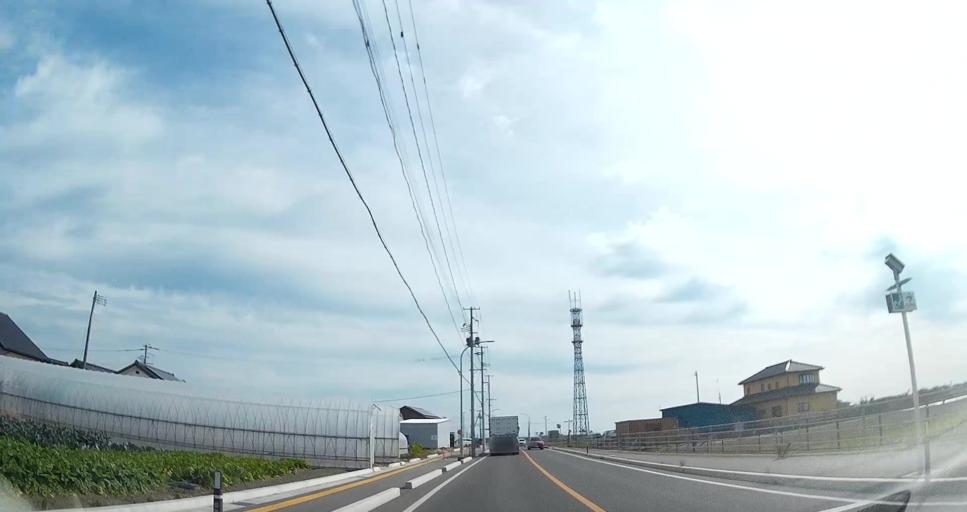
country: JP
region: Miyagi
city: Sendai
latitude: 38.1999
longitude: 140.9500
